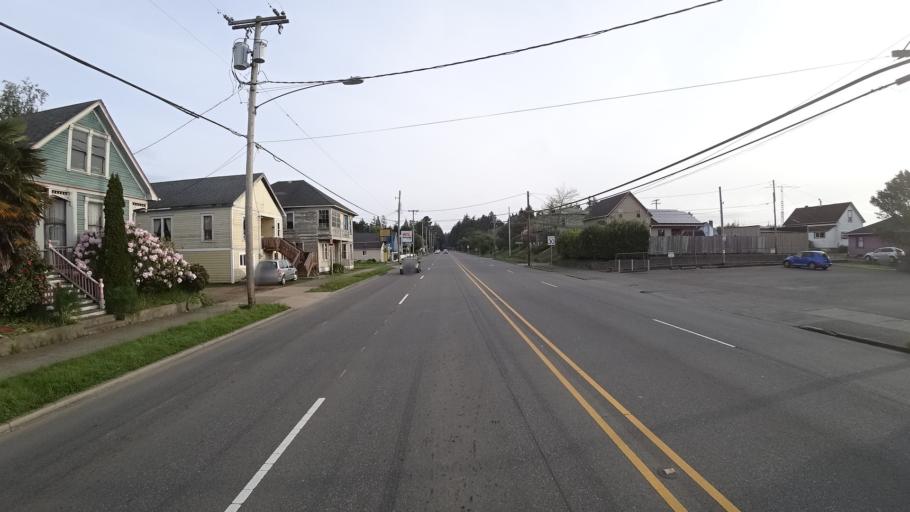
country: US
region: Oregon
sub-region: Coos County
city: North Bend
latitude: 43.4124
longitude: -124.2241
